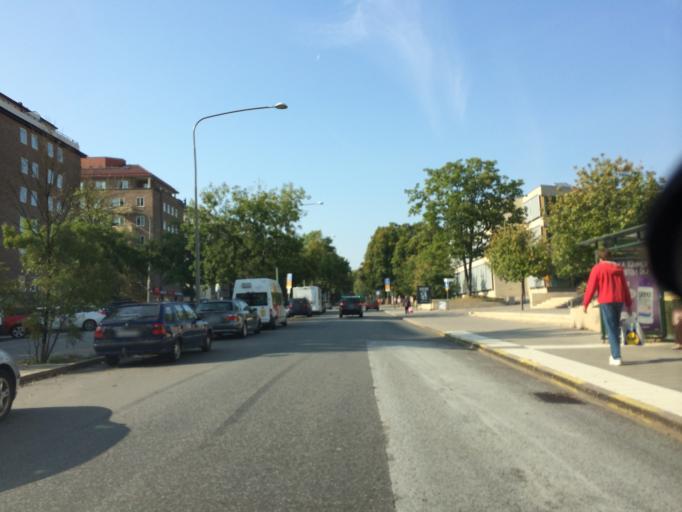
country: SE
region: Stockholm
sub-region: Solna Kommun
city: Solna
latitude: 59.3285
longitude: 18.0154
